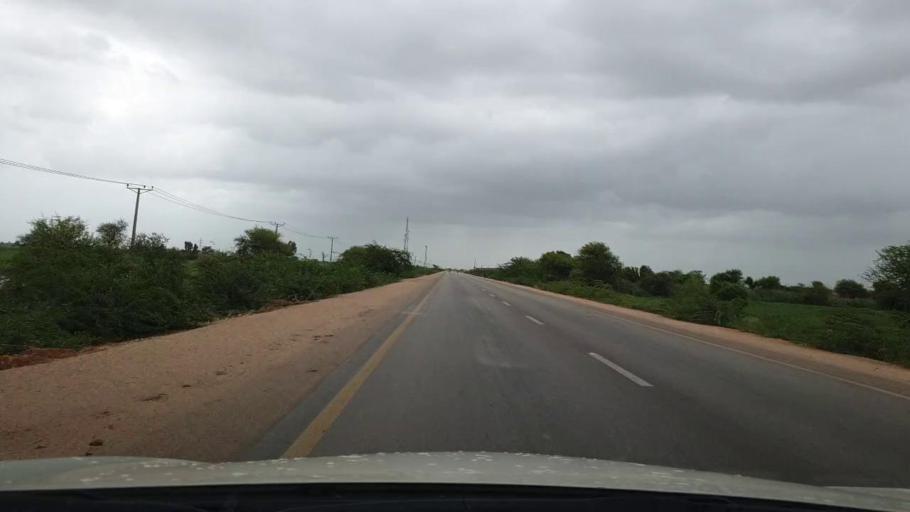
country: PK
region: Sindh
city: Badin
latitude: 24.6550
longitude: 68.7404
